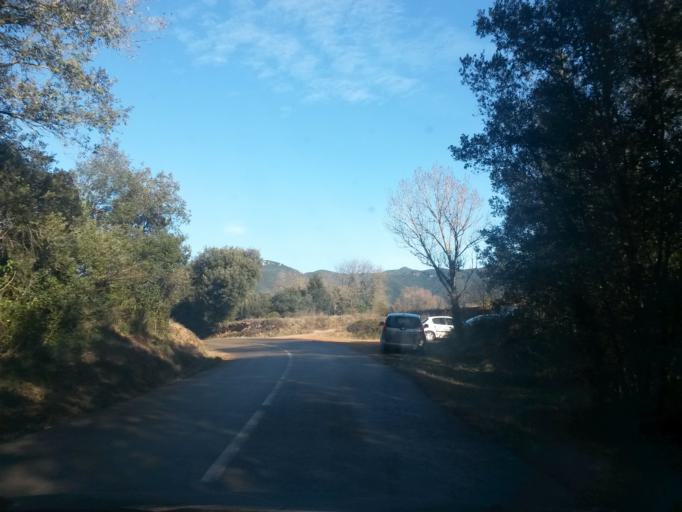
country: ES
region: Catalonia
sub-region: Provincia de Girona
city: la Cellera de Ter
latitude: 42.0184
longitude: 2.6701
